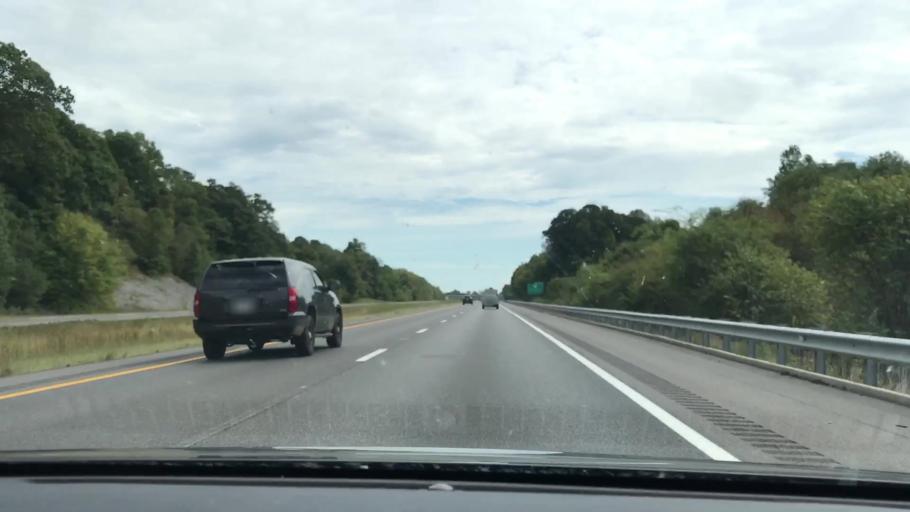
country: US
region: Kentucky
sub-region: Lyon County
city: Eddyville
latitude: 37.0656
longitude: -88.0585
